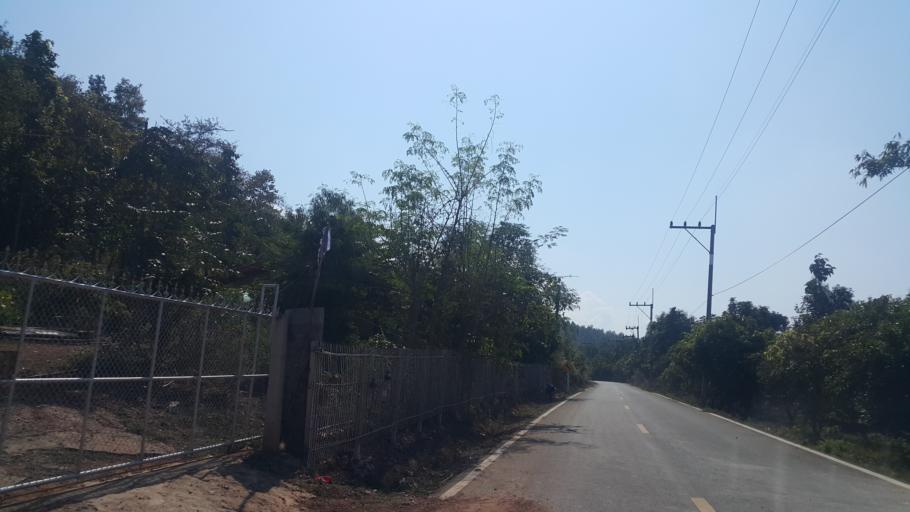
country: TH
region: Chiang Mai
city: San Kamphaeng
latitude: 18.6920
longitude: 99.1693
